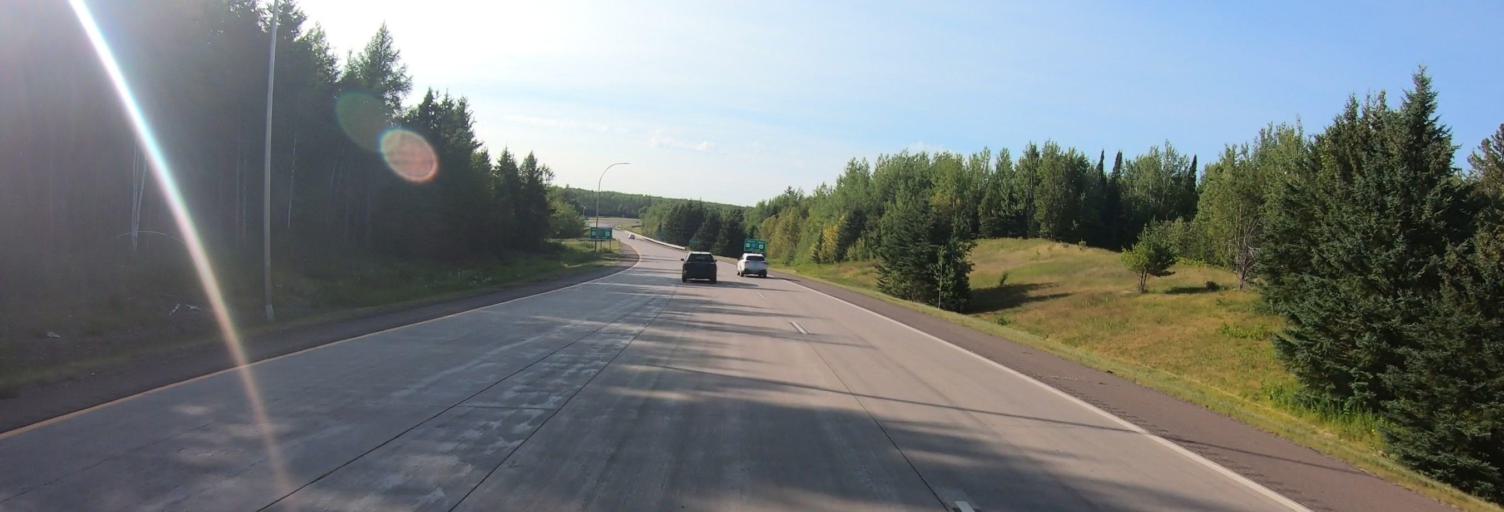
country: US
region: Minnesota
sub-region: Carlton County
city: Cloquet
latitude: 46.9576
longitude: -92.4565
